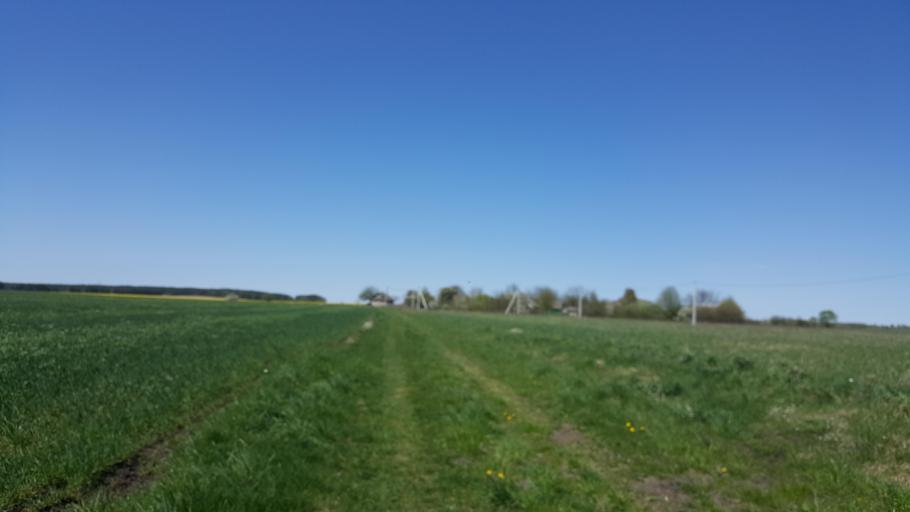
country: BY
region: Brest
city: Charnawchytsy
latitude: 52.3184
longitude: 23.7107
